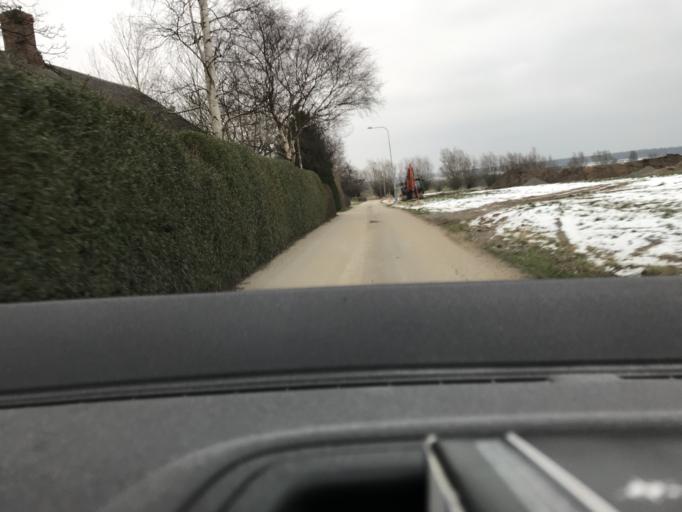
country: SE
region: Skane
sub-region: Ystads Kommun
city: Ystad
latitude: 55.4543
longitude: 13.8599
